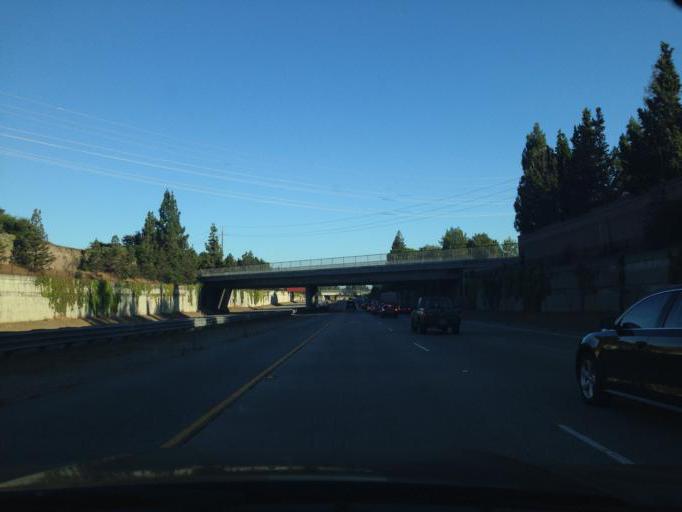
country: US
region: California
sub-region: Santa Clara County
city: Saratoga
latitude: 37.2817
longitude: -122.0138
